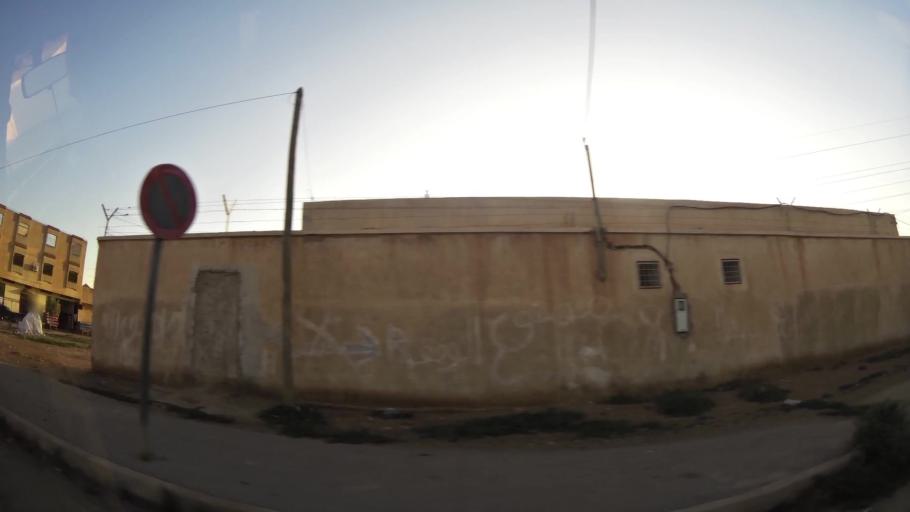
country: MA
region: Oriental
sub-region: Oujda-Angad
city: Oujda
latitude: 34.7114
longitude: -1.9147
